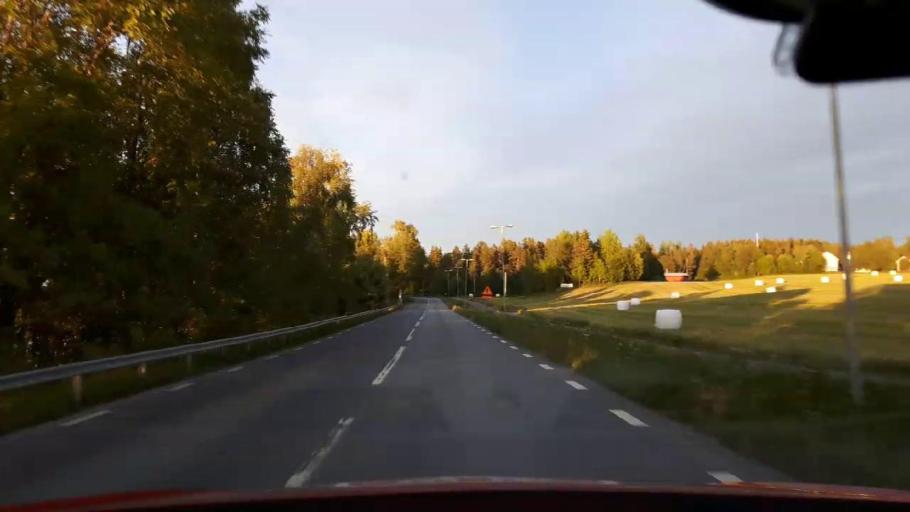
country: SE
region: Jaemtland
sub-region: OEstersunds Kommun
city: Ostersund
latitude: 63.1531
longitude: 14.5355
